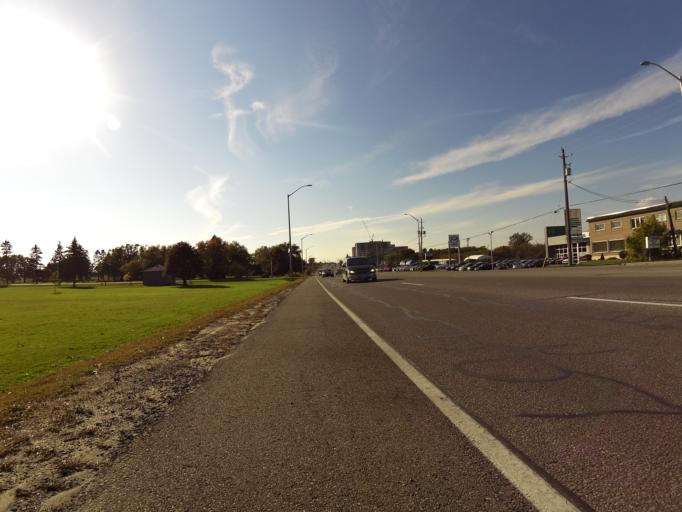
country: CA
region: Ontario
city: Kingston
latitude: 44.2370
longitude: -76.5553
